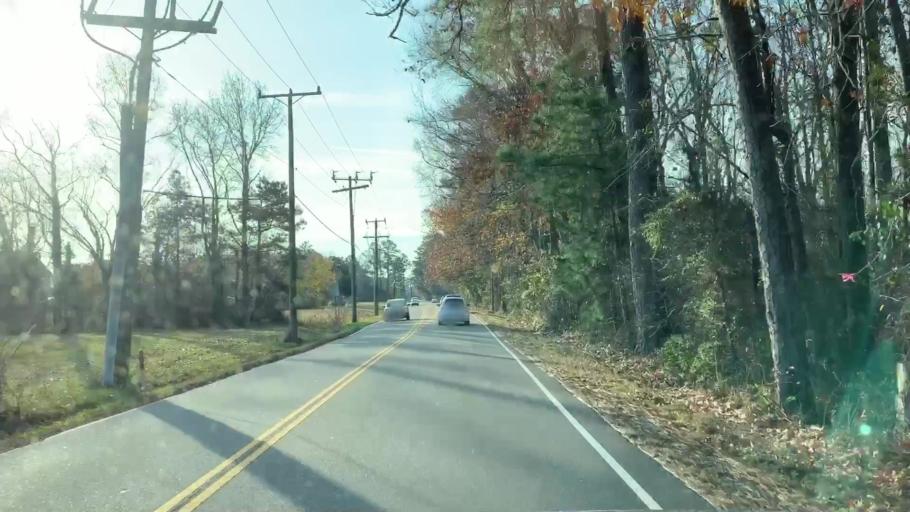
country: US
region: Virginia
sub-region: City of Chesapeake
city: Chesapeake
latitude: 36.7786
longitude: -76.1574
